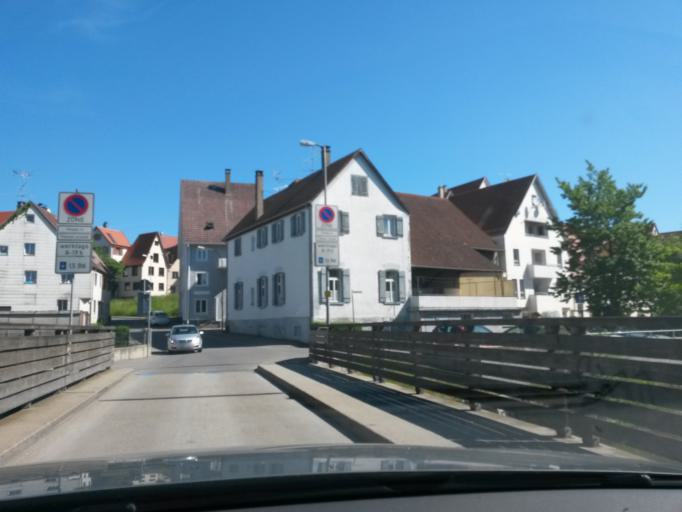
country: DE
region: Baden-Wuerttemberg
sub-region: Tuebingen Region
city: Riedlingen
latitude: 48.1515
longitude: 9.4735
